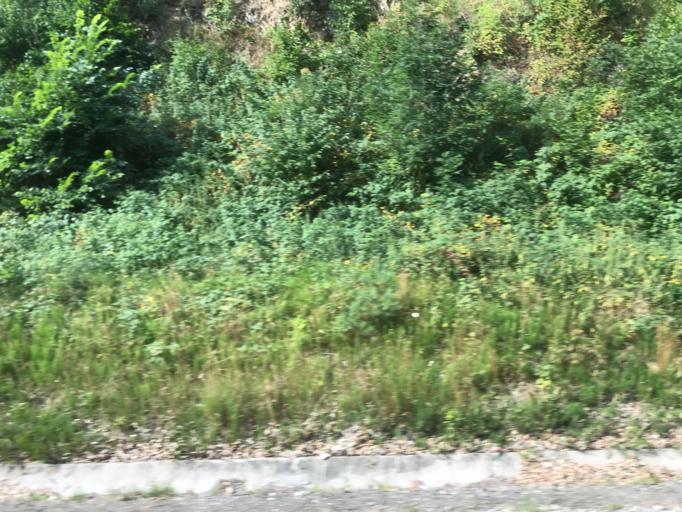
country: CZ
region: Central Bohemia
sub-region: Okres Benesov
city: Cercany
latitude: 49.8281
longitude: 14.7024
